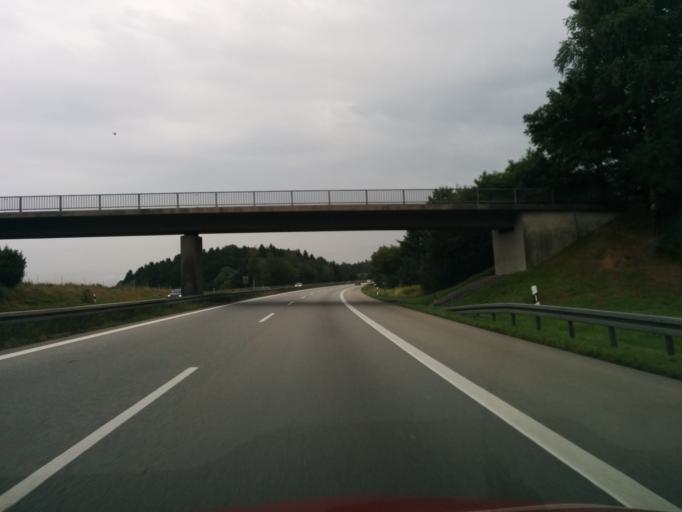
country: DE
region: Bavaria
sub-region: Lower Bavaria
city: Aussernzell
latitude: 48.7042
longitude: 13.1814
